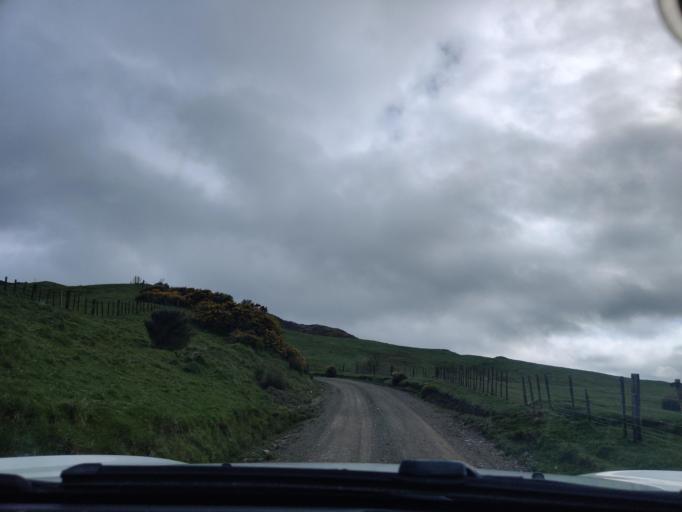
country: NZ
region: Manawatu-Wanganui
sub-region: Palmerston North City
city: Palmerston North
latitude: -40.2805
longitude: 175.8567
